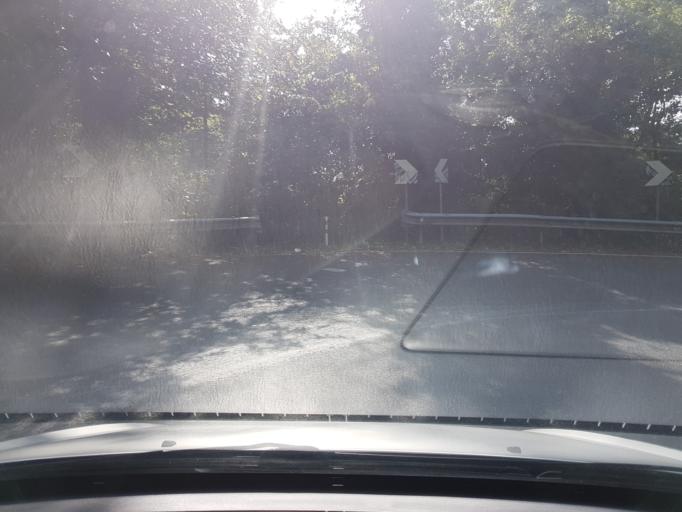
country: IT
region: Friuli Venezia Giulia
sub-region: Provincia di Trieste
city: Sistiana-Visogliano
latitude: 45.7687
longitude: 13.6340
